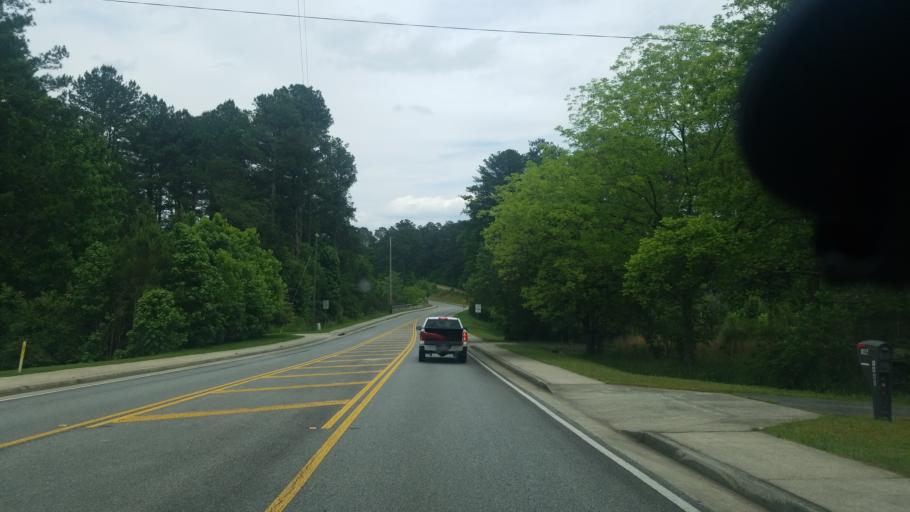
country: US
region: Georgia
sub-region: Forsyth County
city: Cumming
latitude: 34.1947
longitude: -84.1090
